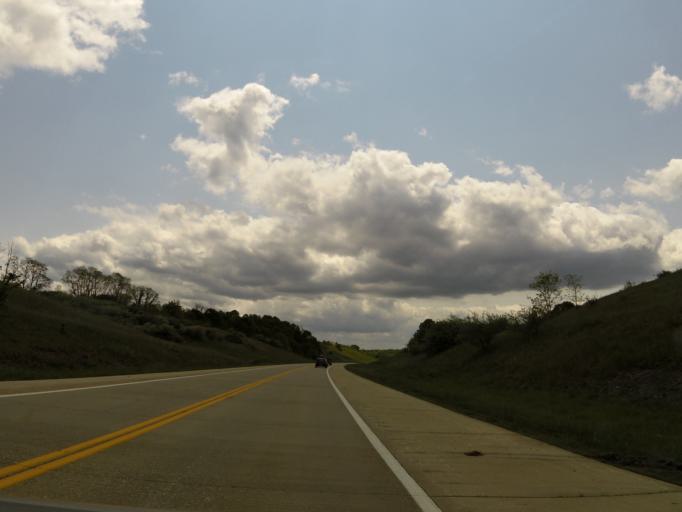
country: US
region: Ohio
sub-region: Athens County
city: Athens
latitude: 39.2294
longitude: -82.0677
